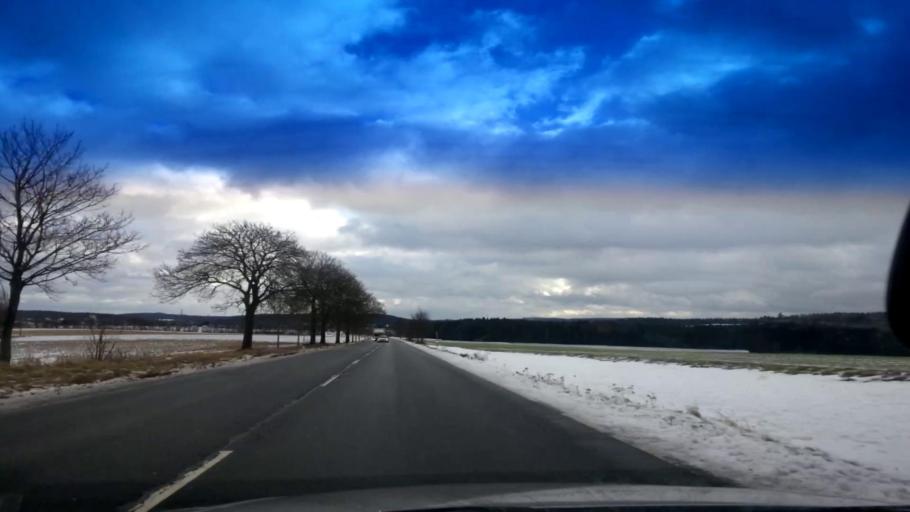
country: DE
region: Bavaria
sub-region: Upper Franconia
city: Kirchenlamitz
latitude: 50.1354
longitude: 11.9730
